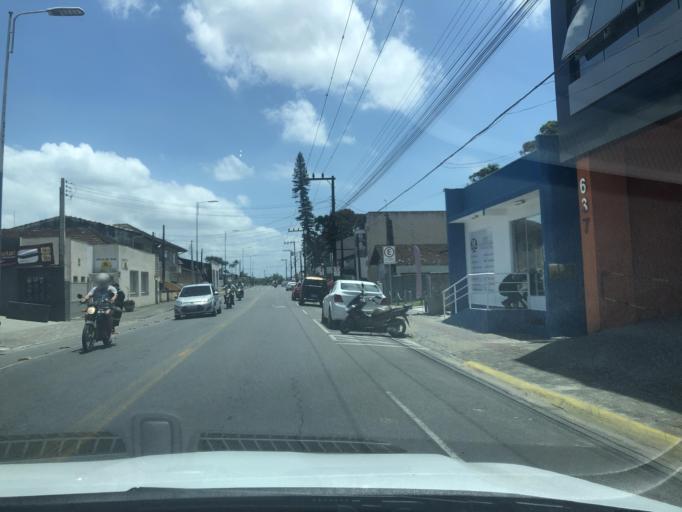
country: BR
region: Santa Catarina
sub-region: Sao Francisco Do Sul
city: Sao Francisco do Sul
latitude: -26.2471
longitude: -48.6361
